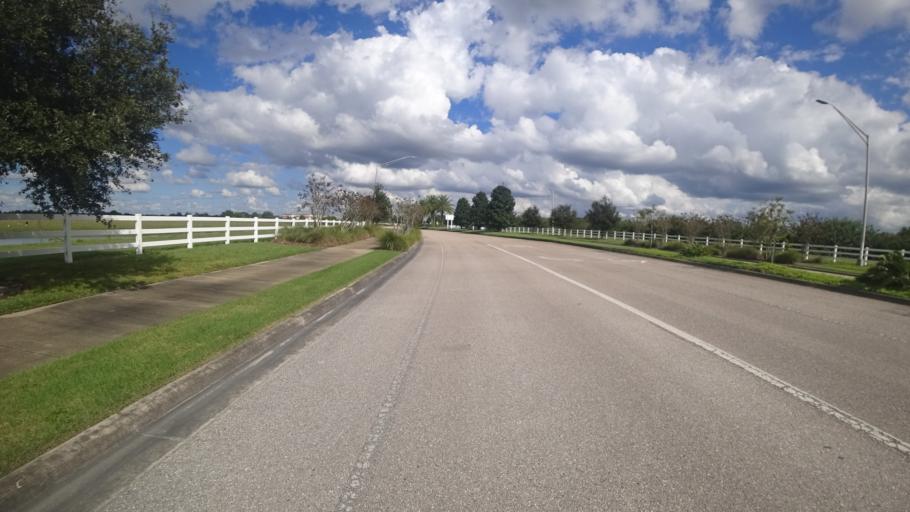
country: US
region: Florida
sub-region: Sarasota County
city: The Meadows
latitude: 27.3960
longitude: -82.3971
